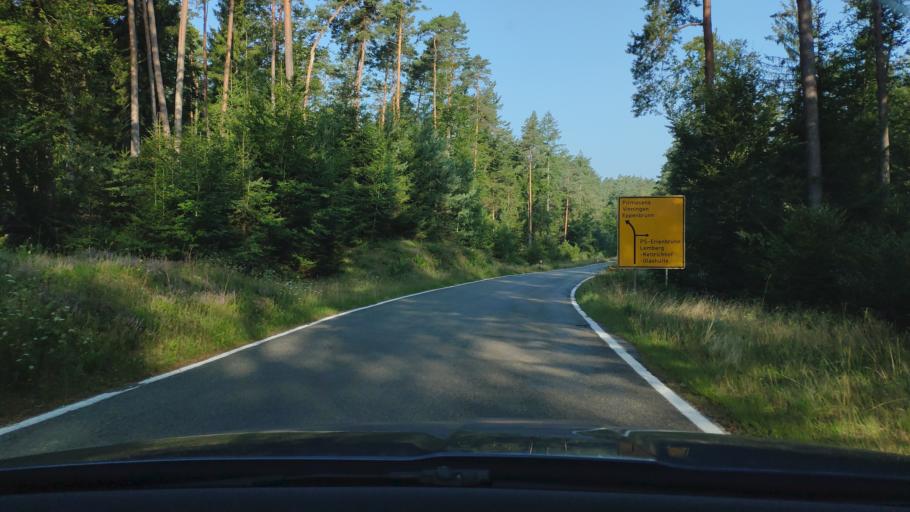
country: DE
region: Rheinland-Pfalz
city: Eppenbrunn
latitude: 49.1118
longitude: 7.5835
